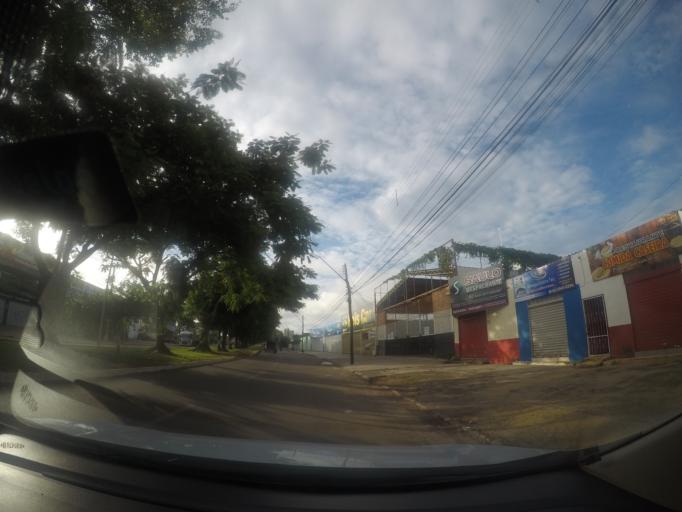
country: BR
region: Goias
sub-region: Goiania
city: Goiania
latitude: -16.6842
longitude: -49.3106
